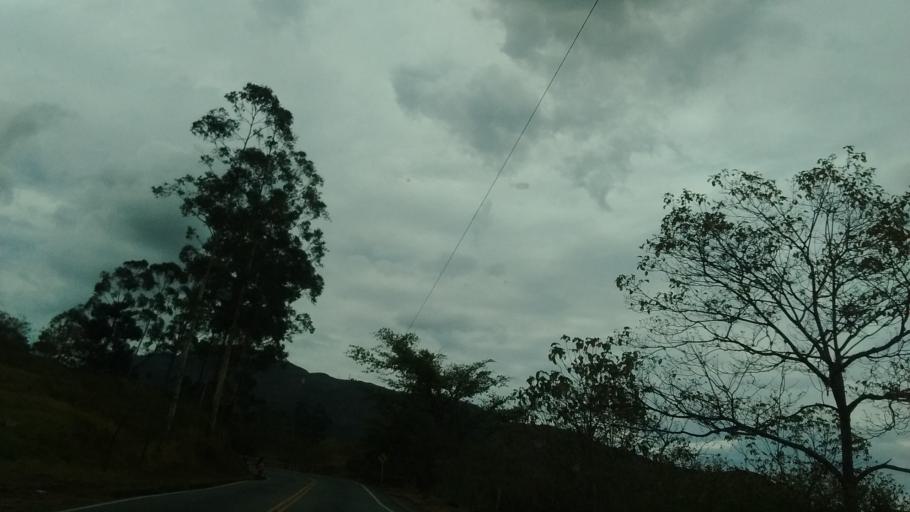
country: CO
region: Cauca
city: Rosas
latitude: 2.2816
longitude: -76.7207
